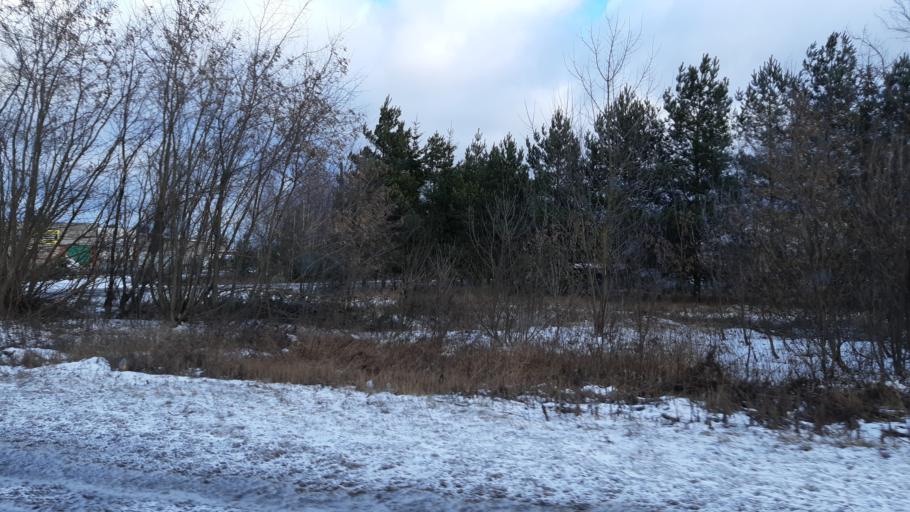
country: RU
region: Moskovskaya
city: Noginsk-9
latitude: 56.0143
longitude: 38.5581
